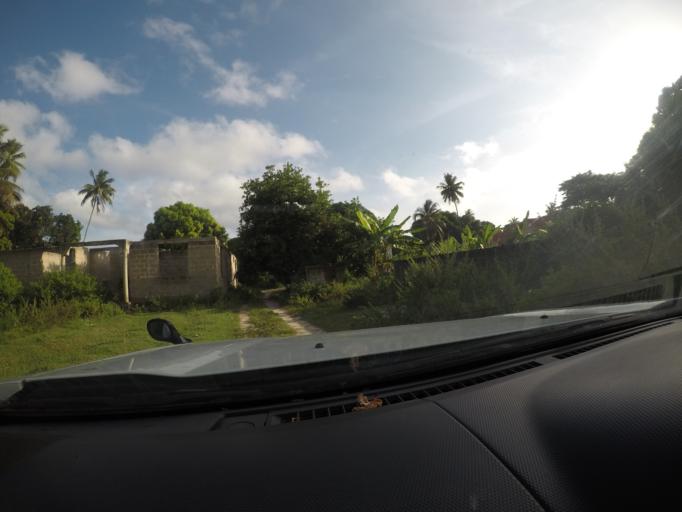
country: TZ
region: Pemba South
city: Chake Chake
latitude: -5.2481
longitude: 39.7862
